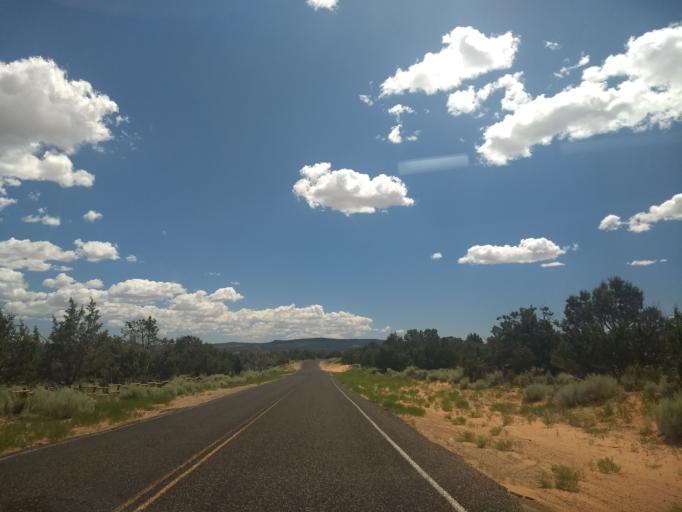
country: US
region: Utah
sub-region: Kane County
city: Kanab
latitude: 37.0384
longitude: -112.7313
